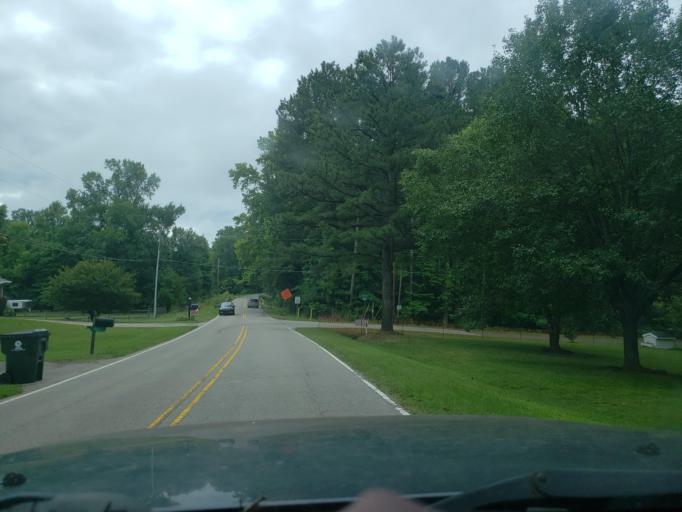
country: US
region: North Carolina
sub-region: Durham County
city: Gorman
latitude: 35.9678
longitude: -78.7841
